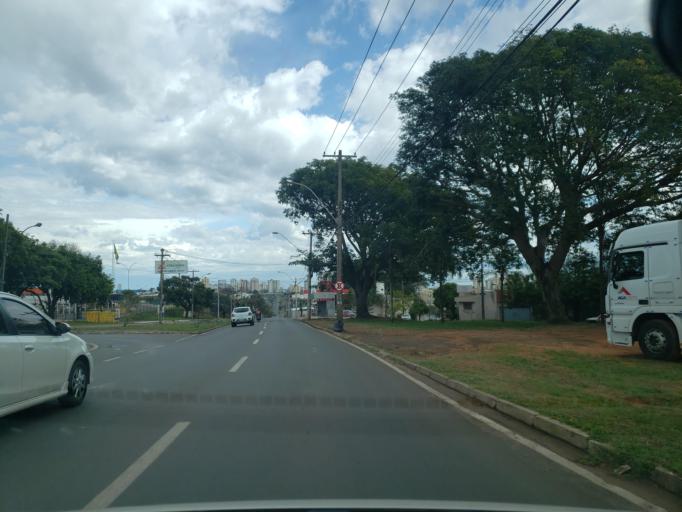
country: BR
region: Sao Paulo
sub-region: Bauru
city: Bauru
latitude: -22.3352
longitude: -49.0317
